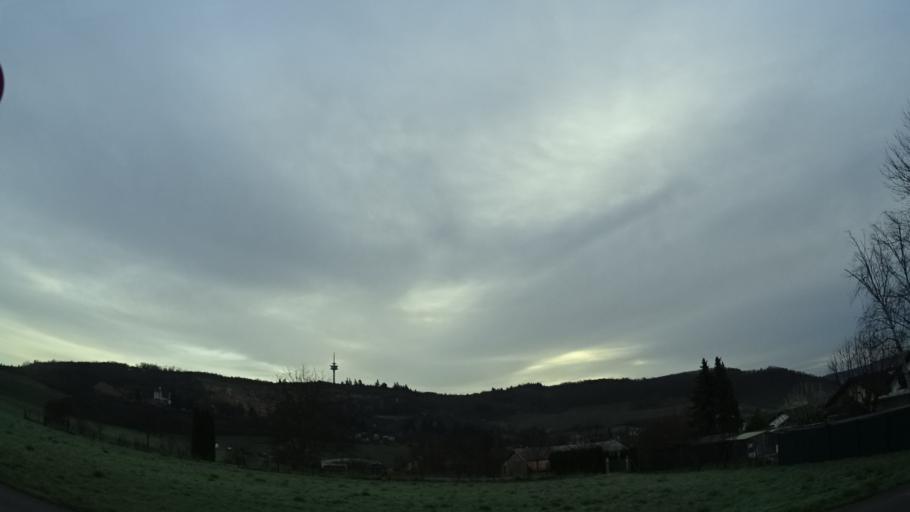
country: DE
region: Rheinland-Pfalz
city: Traisen
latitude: 49.8215
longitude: 7.8136
